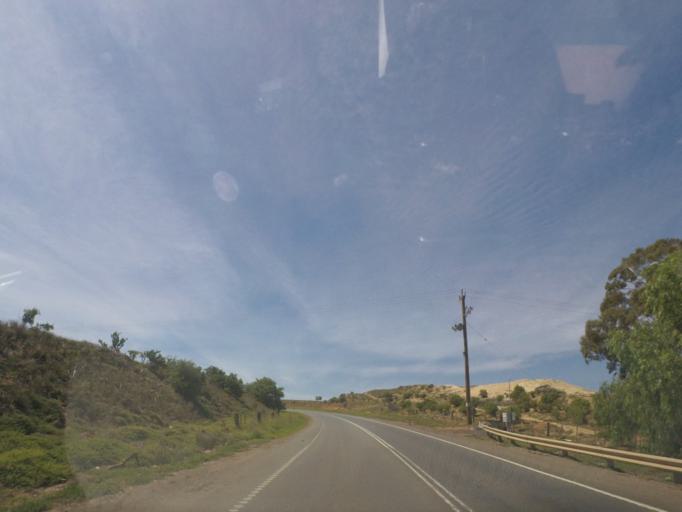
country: AU
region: Victoria
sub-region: Moorabool
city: Bacchus Marsh
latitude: -37.6988
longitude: 144.4509
